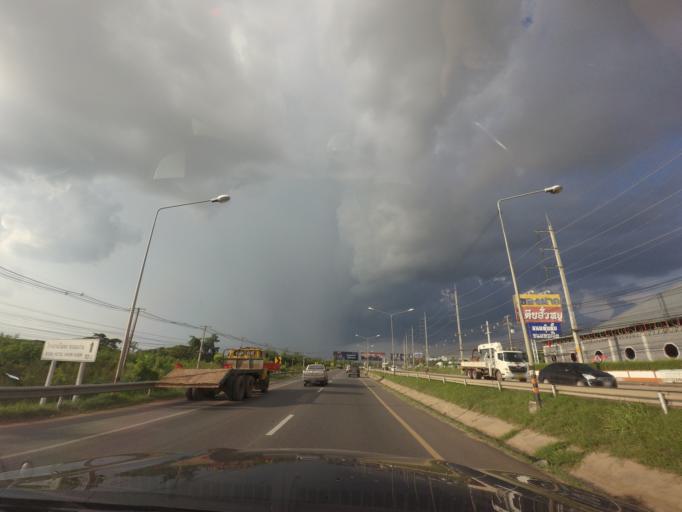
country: TH
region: Khon Kaen
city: Khon Kaen
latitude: 16.3619
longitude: 102.8049
